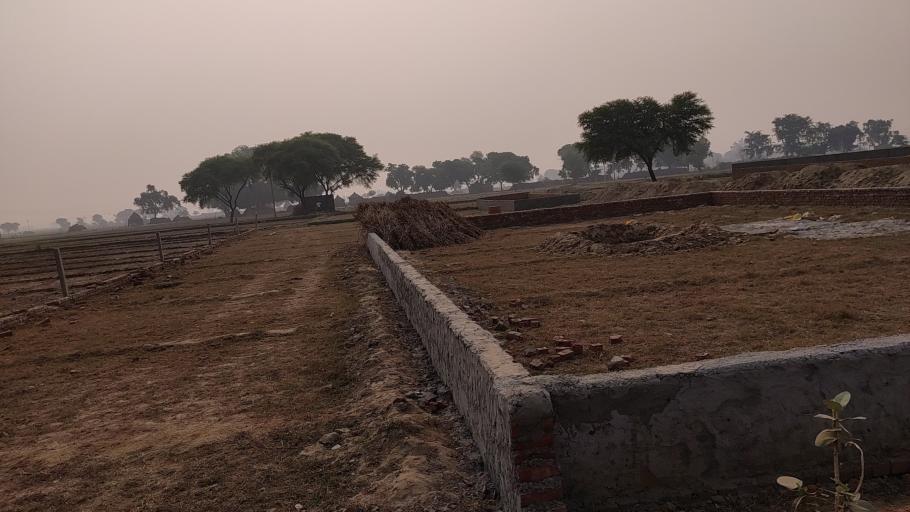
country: IN
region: Uttar Pradesh
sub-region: Mathura
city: Vrindavan
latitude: 27.5534
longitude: 77.7143
